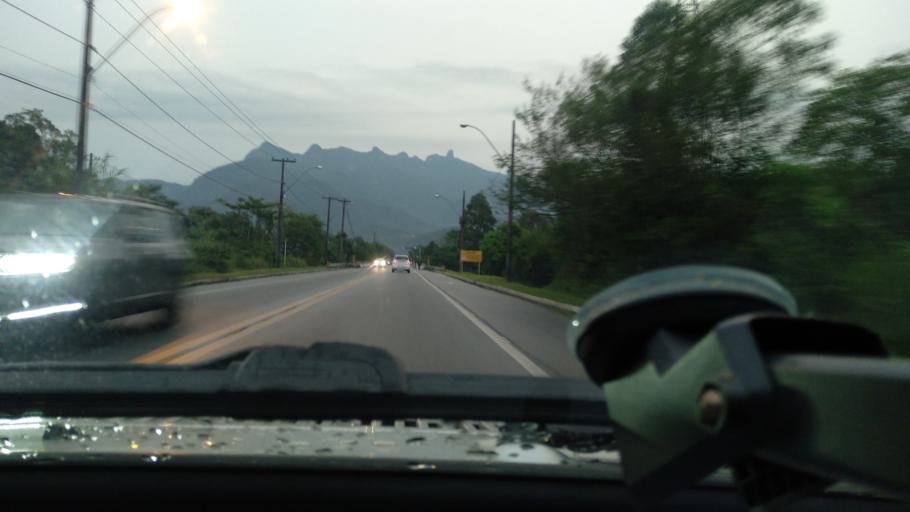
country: BR
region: Rio de Janeiro
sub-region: Angra Dos Reis
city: Angra dos Reis
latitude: -23.0261
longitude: -44.5381
